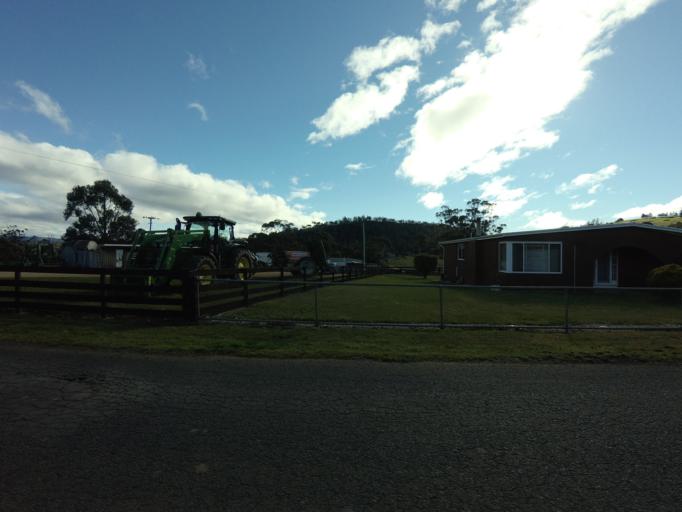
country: AU
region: Tasmania
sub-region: Derwent Valley
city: New Norfolk
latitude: -42.7256
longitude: 147.0314
